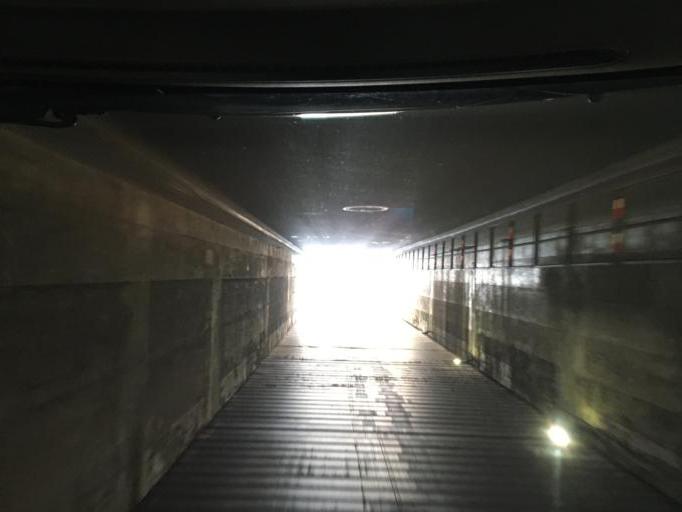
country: DE
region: Lower Saxony
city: Uelzen
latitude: 52.9627
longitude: 10.5438
